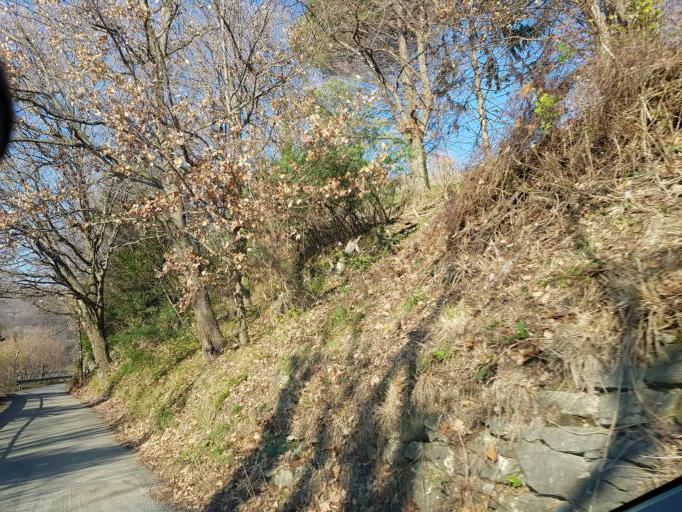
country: IT
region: Liguria
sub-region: Provincia di Genova
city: Santa Marta
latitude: 44.4902
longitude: 8.8891
